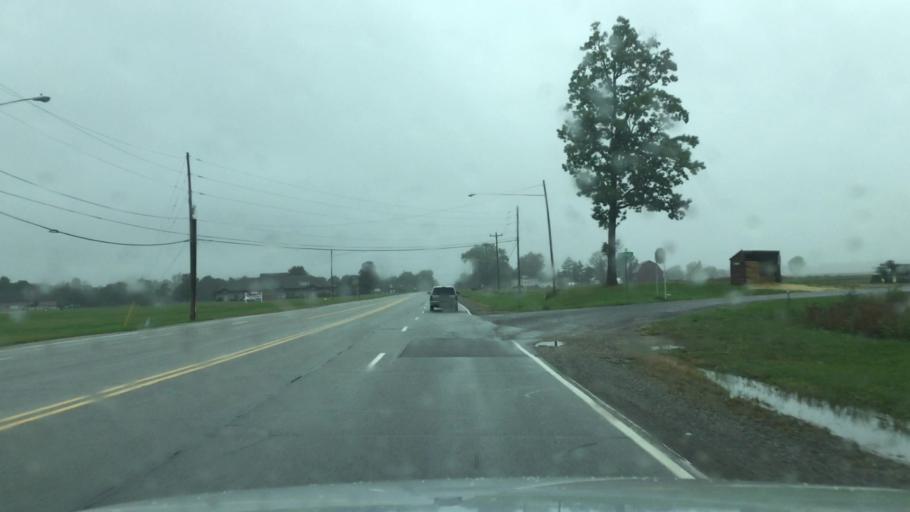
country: US
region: Michigan
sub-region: Saginaw County
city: Bridgeport
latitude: 43.3359
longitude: -83.8355
